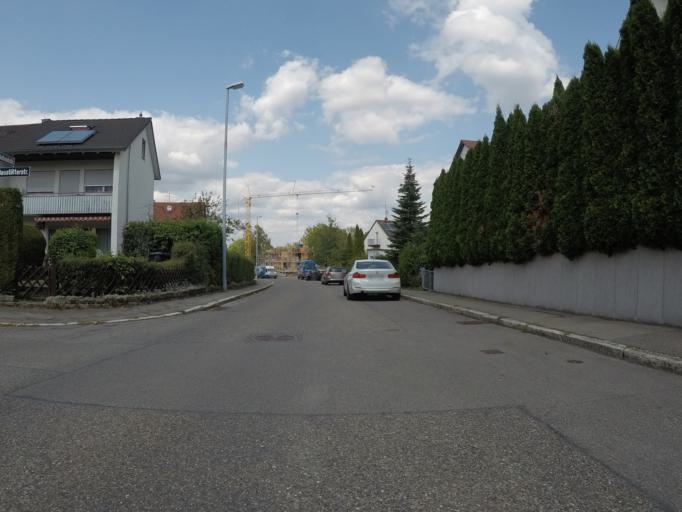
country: DE
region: Baden-Wuerttemberg
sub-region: Tuebingen Region
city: Reutlingen
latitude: 48.4784
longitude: 9.2121
